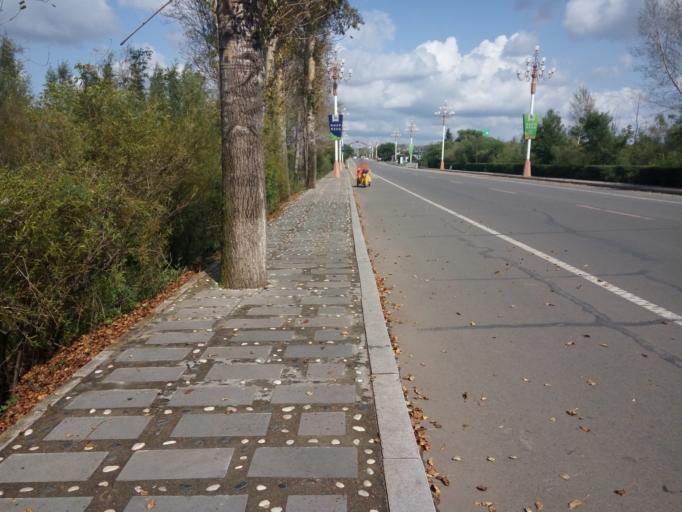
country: CN
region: Heilongjiang Sheng
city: Erjing
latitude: 48.6484
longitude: 126.1460
